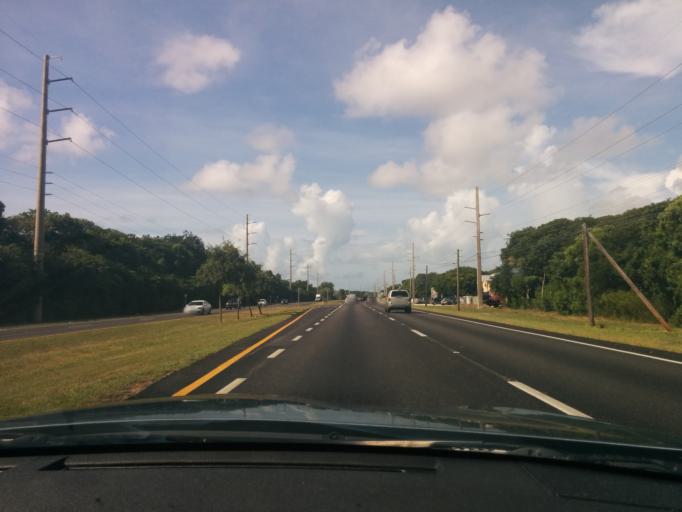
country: US
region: Florida
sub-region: Monroe County
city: Key Largo
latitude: 25.1071
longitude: -80.4282
